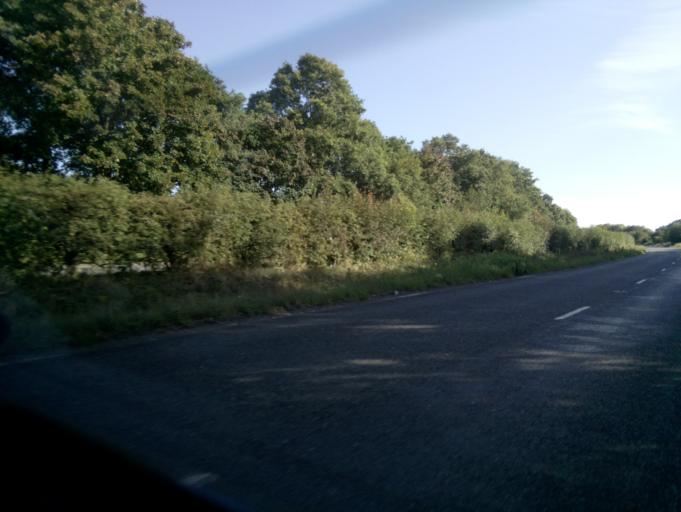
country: GB
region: England
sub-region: Hampshire
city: Romsey
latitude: 50.9742
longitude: -1.5201
